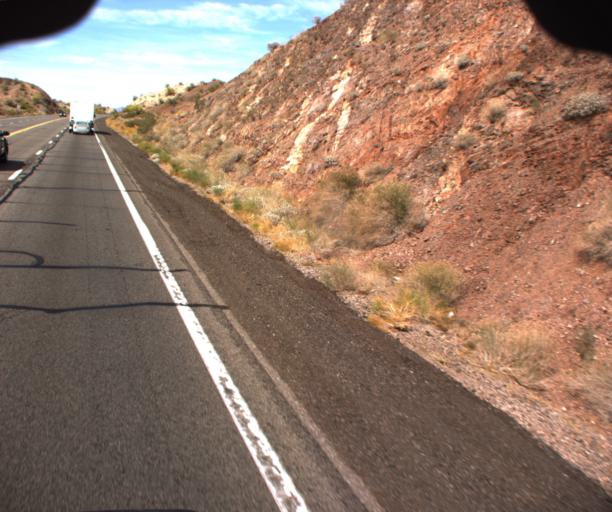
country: US
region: Arizona
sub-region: Mohave County
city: Desert Hills
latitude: 34.6392
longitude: -114.3245
